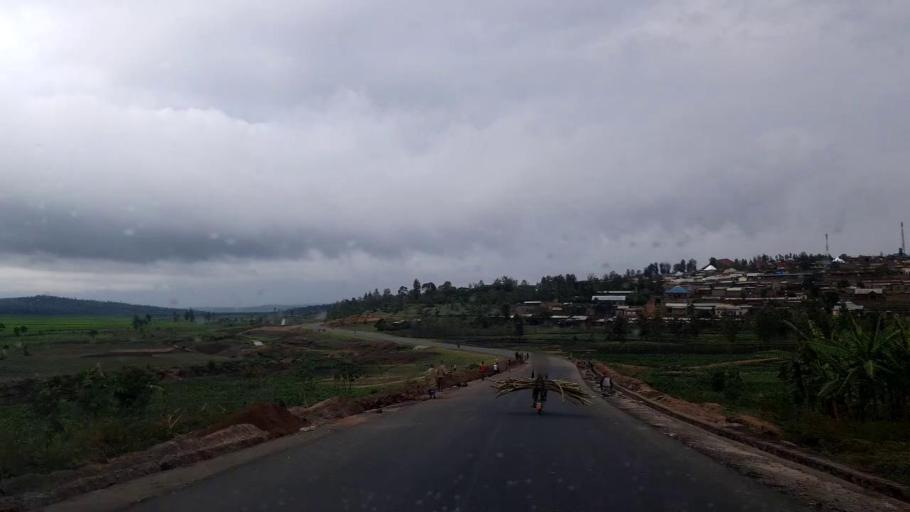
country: RW
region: Northern Province
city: Byumba
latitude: -1.4479
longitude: 30.2476
